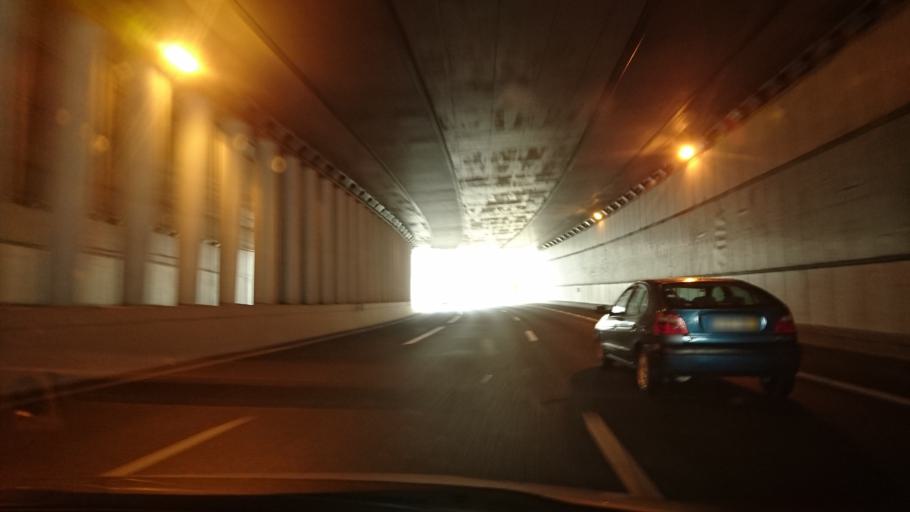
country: PT
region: Porto
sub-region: Gondomar
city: Rio Tinto
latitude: 41.1584
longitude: -8.5673
